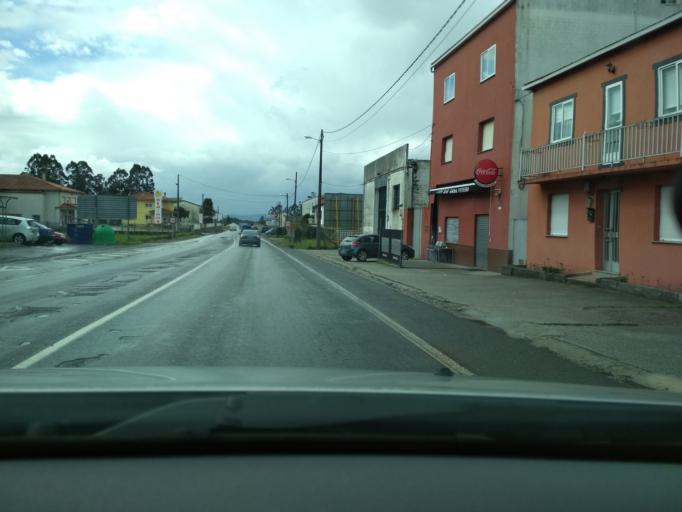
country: ES
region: Galicia
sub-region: Provincia da Coruna
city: Santiago de Compostela
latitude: 42.8372
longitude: -8.5854
